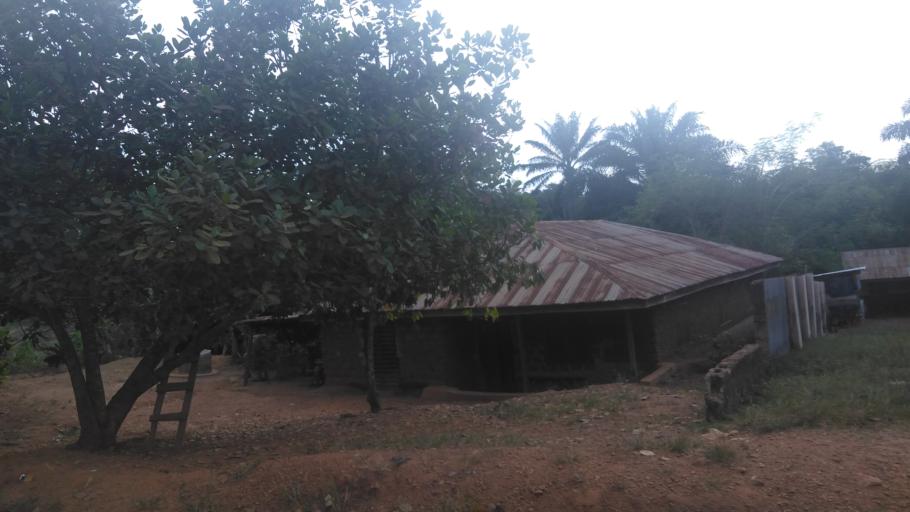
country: NG
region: Osun
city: Ifetedo
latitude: 7.0130
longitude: 4.6352
